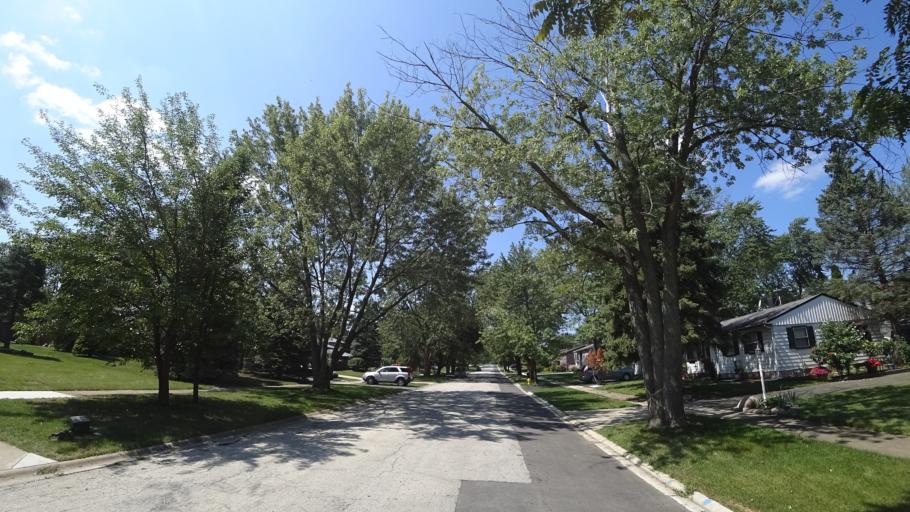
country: US
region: Illinois
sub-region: Cook County
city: Orland Park
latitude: 41.6235
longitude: -87.8384
